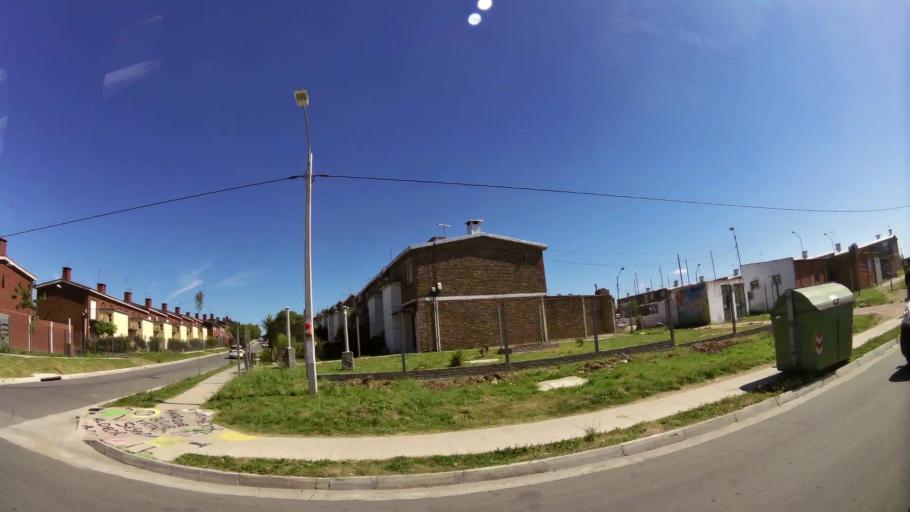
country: UY
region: Canelones
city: Paso de Carrasco
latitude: -34.8607
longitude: -56.1210
